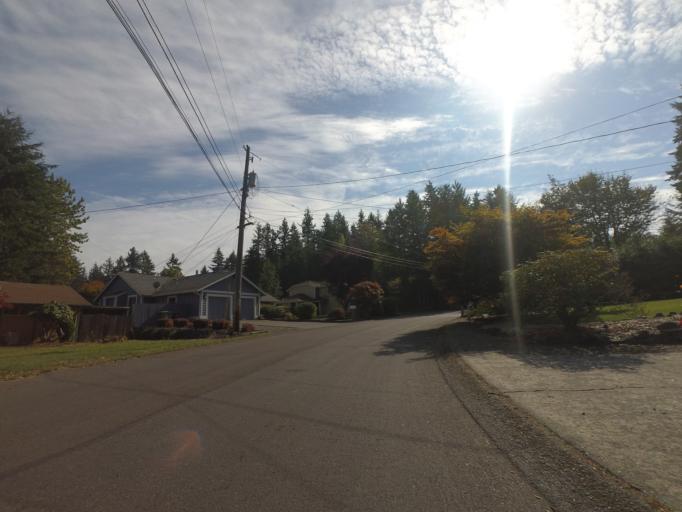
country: US
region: Washington
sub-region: Pierce County
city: Fircrest
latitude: 47.2146
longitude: -122.5287
